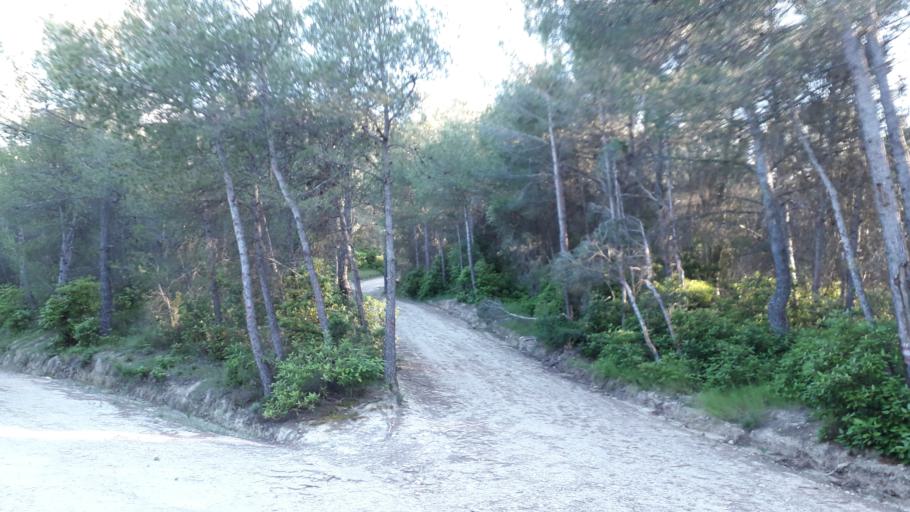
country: ES
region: Catalonia
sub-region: Provincia de Barcelona
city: Orpi
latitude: 41.5563
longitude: 1.5623
